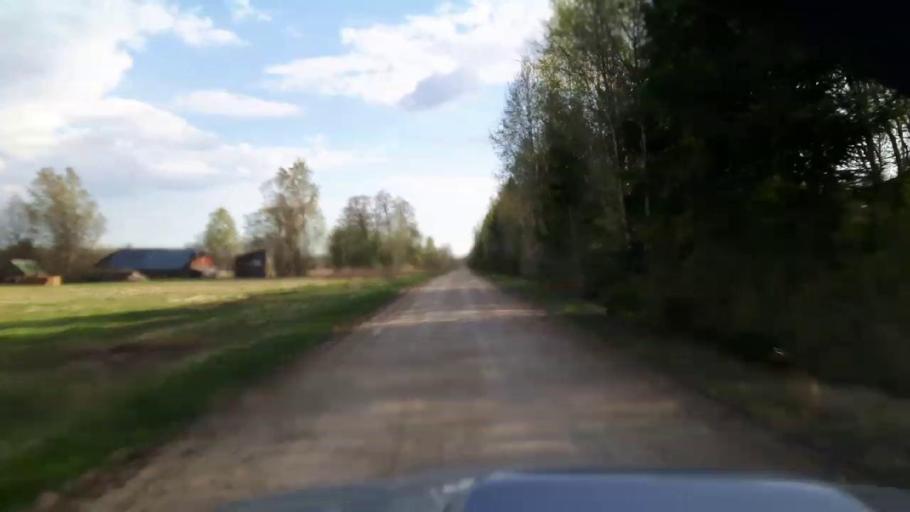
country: EE
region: Paernumaa
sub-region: Tootsi vald
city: Tootsi
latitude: 58.4373
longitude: 24.8093
